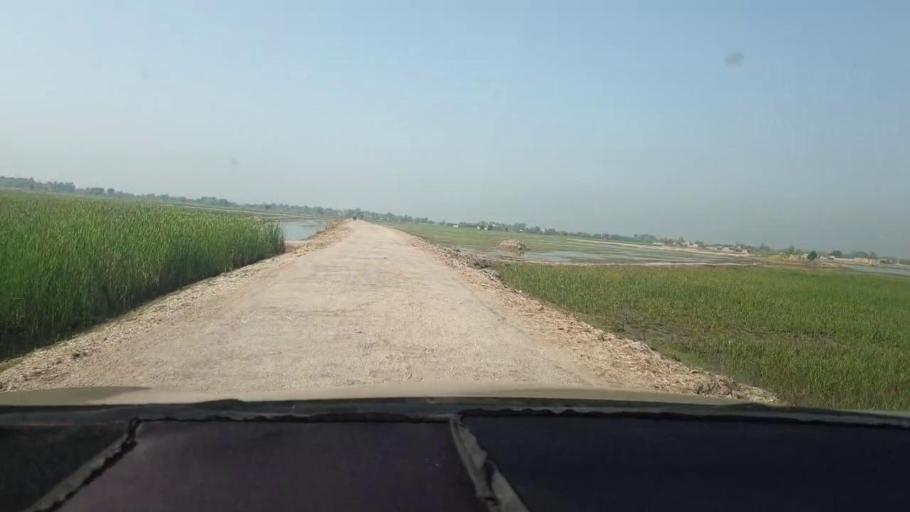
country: PK
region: Sindh
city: Kambar
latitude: 27.5786
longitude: 68.0900
